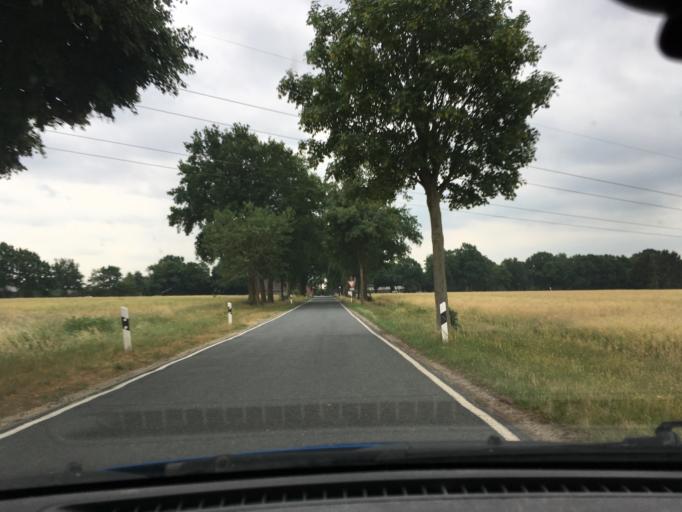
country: DE
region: Lower Saxony
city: Kakenstorf
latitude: 53.3134
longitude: 9.7641
